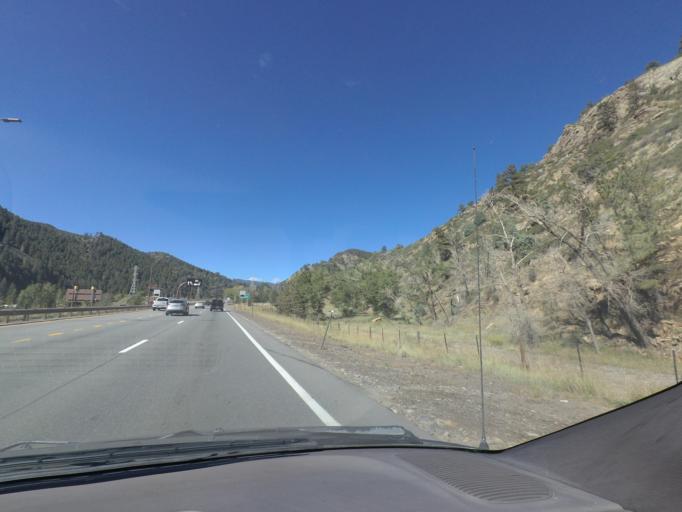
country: US
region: Colorado
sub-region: Clear Creek County
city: Idaho Springs
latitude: 39.7353
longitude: -105.4801
